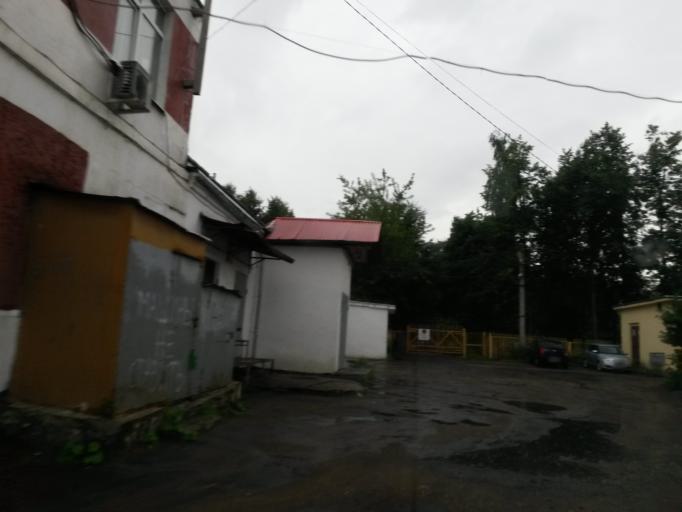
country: RU
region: Jaroslavl
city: Yaroslavl
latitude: 57.6439
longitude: 39.8818
